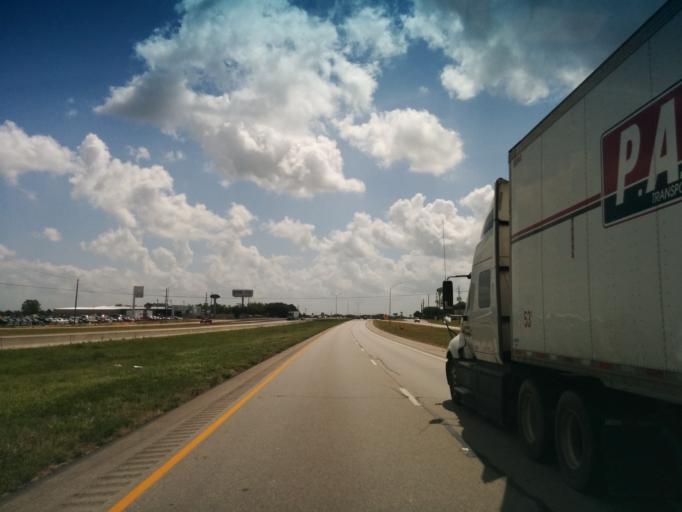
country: US
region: Texas
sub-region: Austin County
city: Sealy
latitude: 29.7746
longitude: -96.1296
